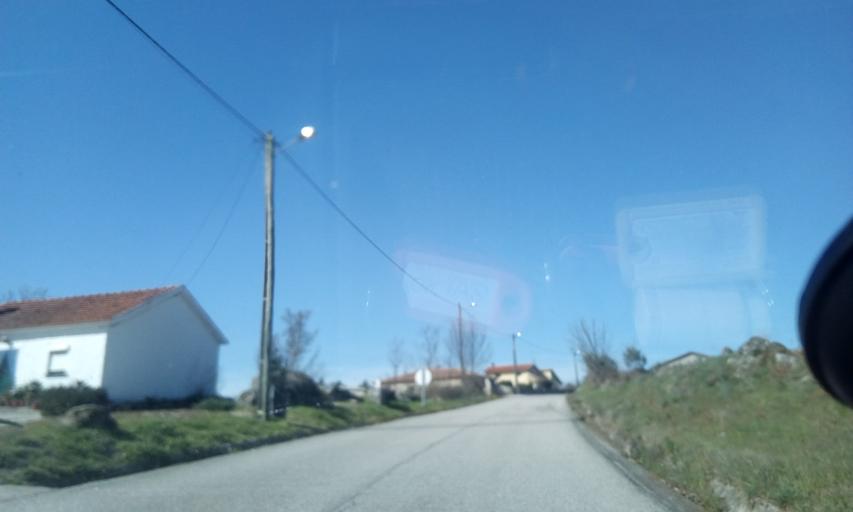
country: PT
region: Guarda
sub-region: Celorico da Beira
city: Celorico da Beira
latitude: 40.5913
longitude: -7.4407
